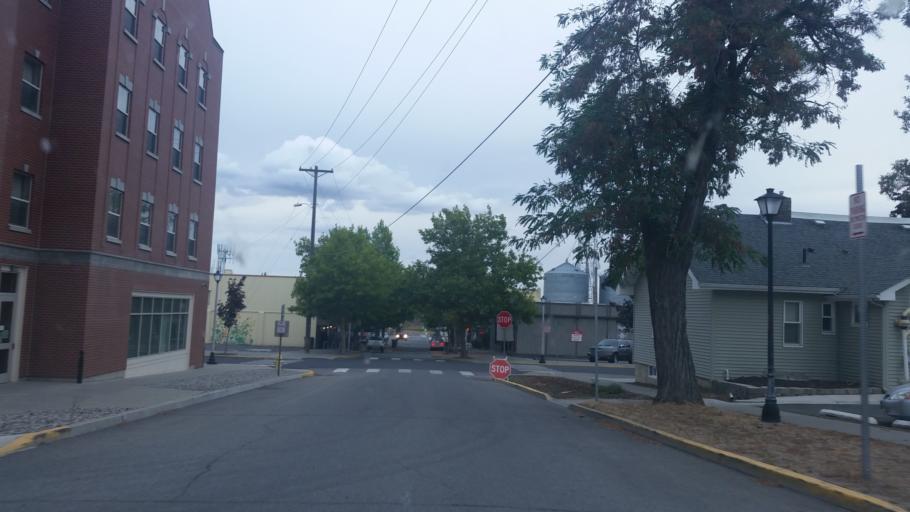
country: US
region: Washington
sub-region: Spokane County
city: Cheney
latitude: 47.4876
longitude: -117.5773
